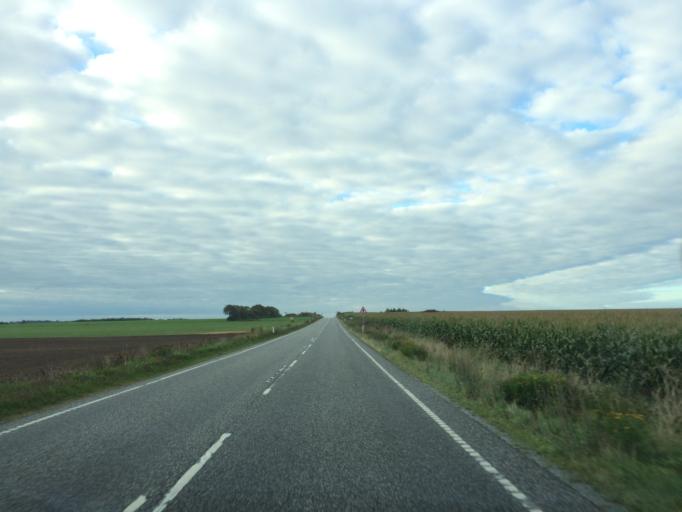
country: DK
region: Central Jutland
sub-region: Ringkobing-Skjern Kommune
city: Skjern
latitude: 56.0071
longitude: 8.5030
